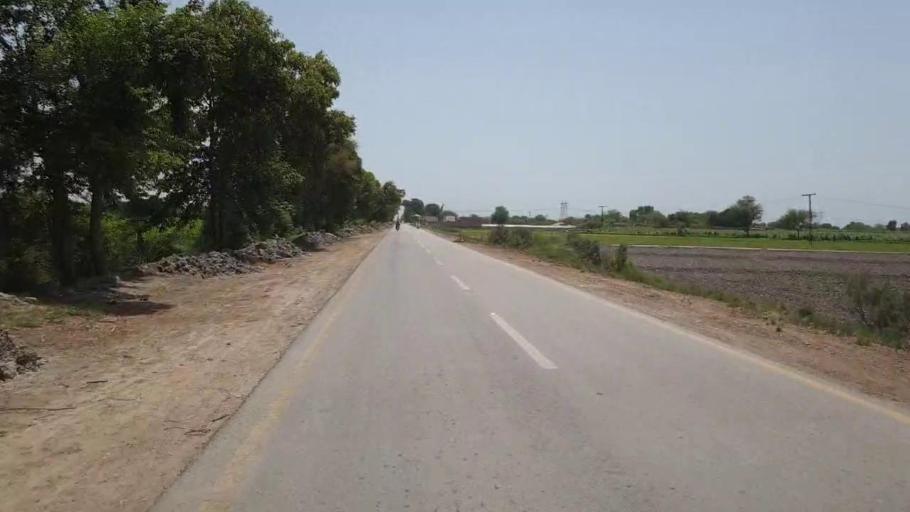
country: PK
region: Sindh
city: Daur
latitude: 26.3483
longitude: 68.1362
